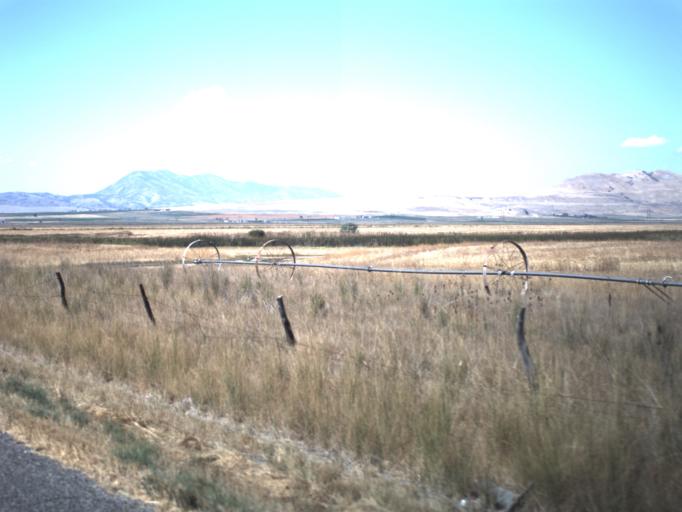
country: US
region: Utah
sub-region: Cache County
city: Benson
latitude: 41.8451
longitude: -111.9163
